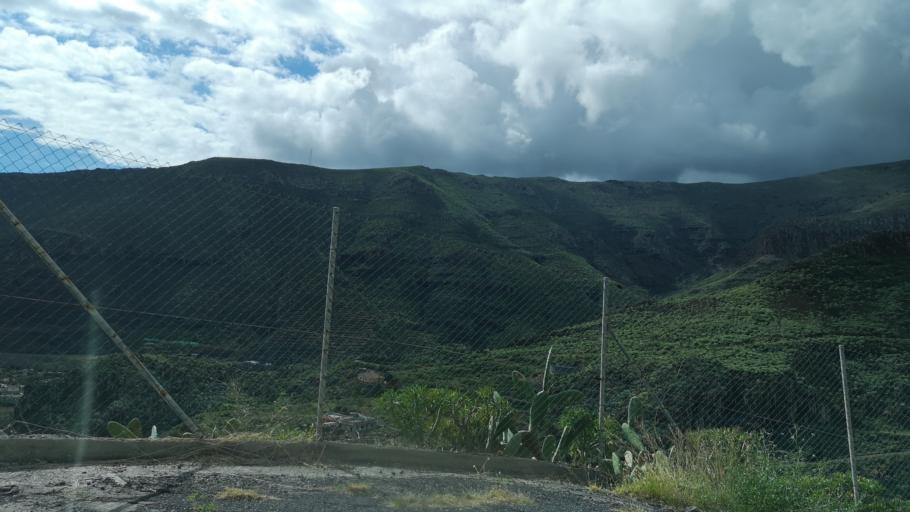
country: ES
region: Canary Islands
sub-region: Provincia de Santa Cruz de Tenerife
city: San Sebastian de la Gomera
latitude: 28.1107
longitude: -17.1293
